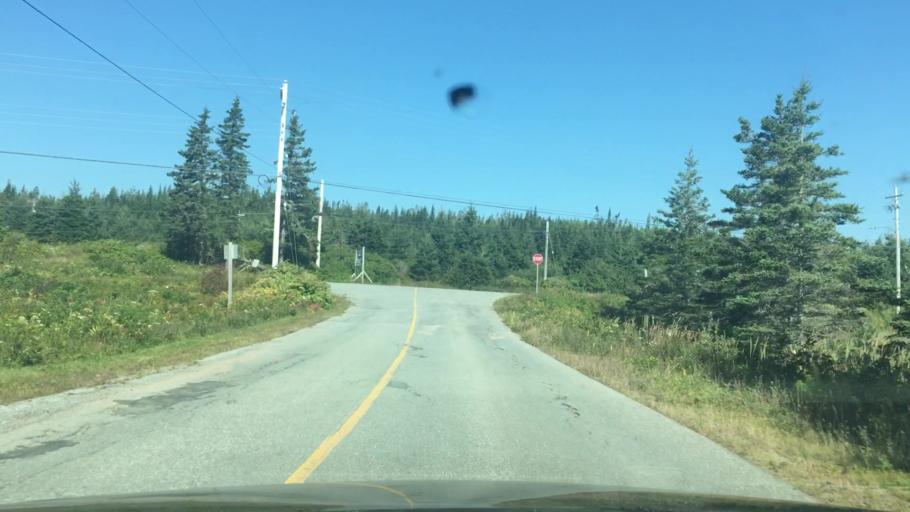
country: CA
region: Nova Scotia
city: New Glasgow
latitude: 44.8047
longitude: -62.6934
